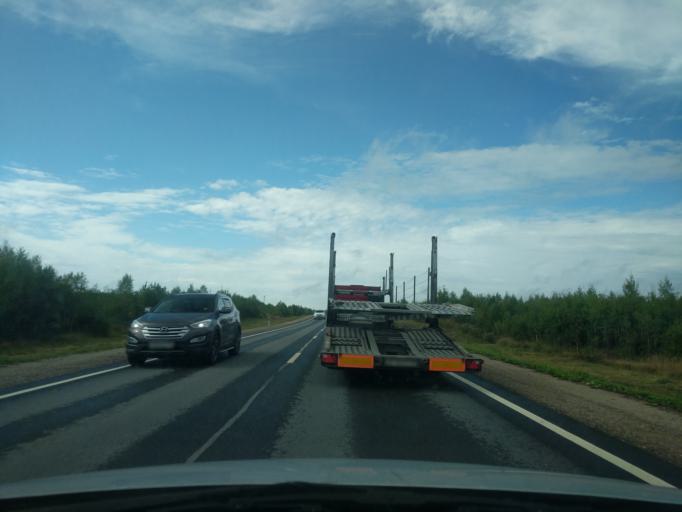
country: RU
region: Kostroma
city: Sudislavl'
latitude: 57.8205
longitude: 41.9156
